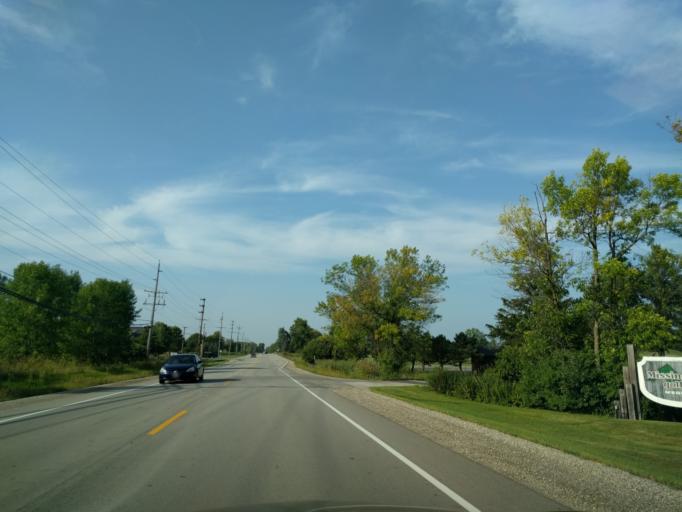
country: US
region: Wisconsin
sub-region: Ozaukee County
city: Thiensville
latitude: 43.2532
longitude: -87.9240
